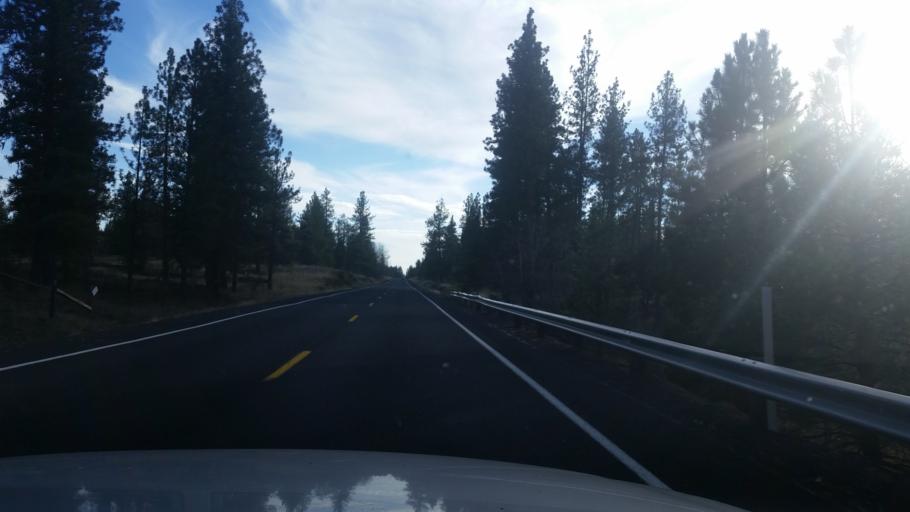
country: US
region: Washington
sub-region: Spokane County
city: Cheney
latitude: 47.4133
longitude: -117.5683
